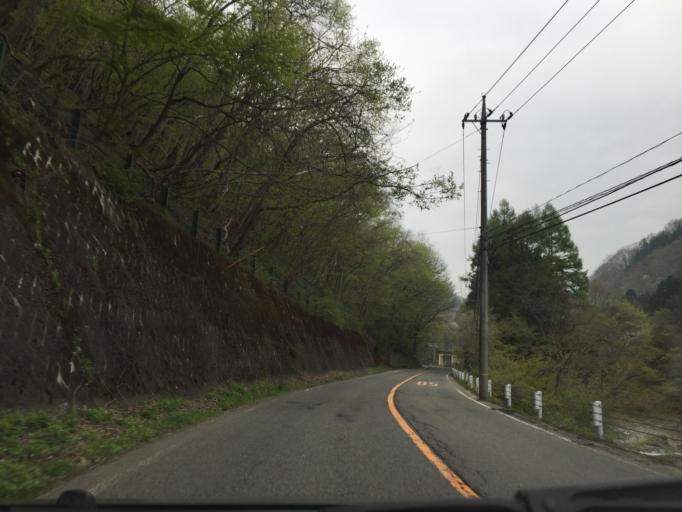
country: JP
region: Tochigi
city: Nikko
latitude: 36.9929
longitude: 139.7104
